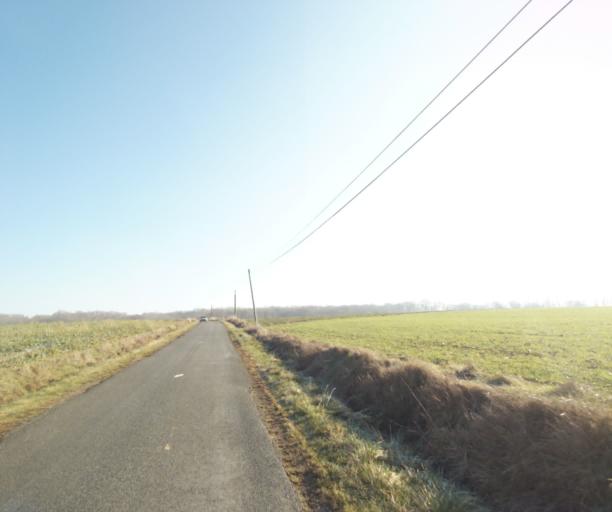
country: FR
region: Champagne-Ardenne
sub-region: Departement de la Haute-Marne
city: Bienville
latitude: 48.5091
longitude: 5.0202
